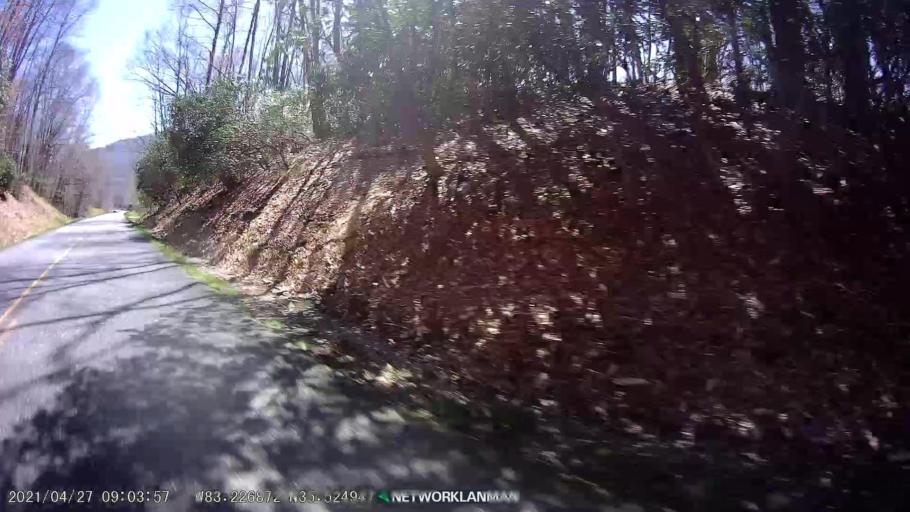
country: US
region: North Carolina
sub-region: Swain County
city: Cherokee
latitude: 35.5249
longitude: -83.2265
